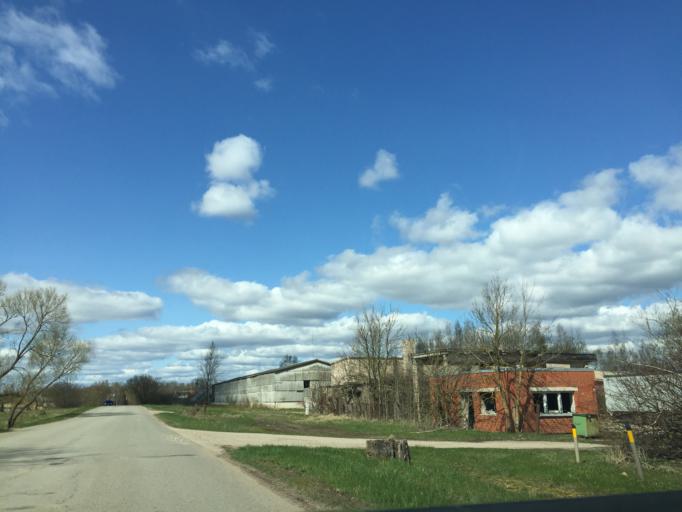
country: LV
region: Vilanu
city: Vilani
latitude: 56.7303
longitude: 27.0733
